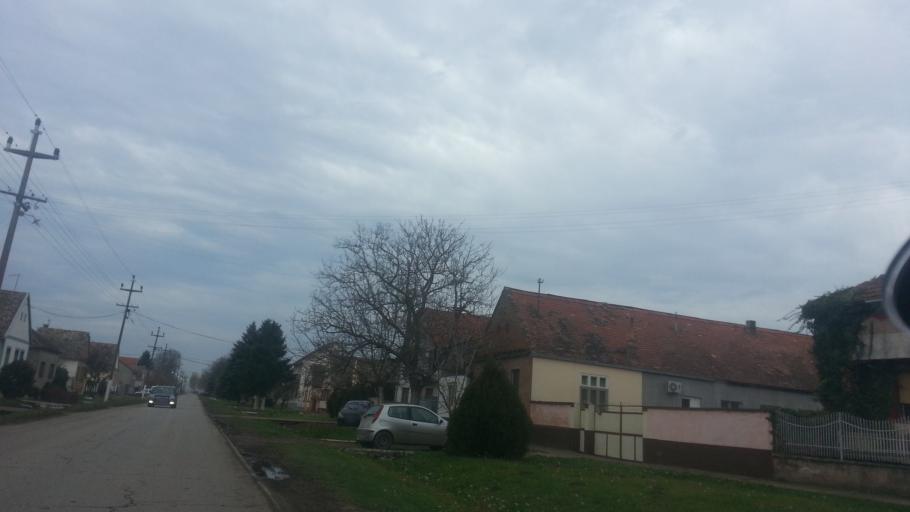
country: RS
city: Golubinci
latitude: 44.9933
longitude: 20.0615
